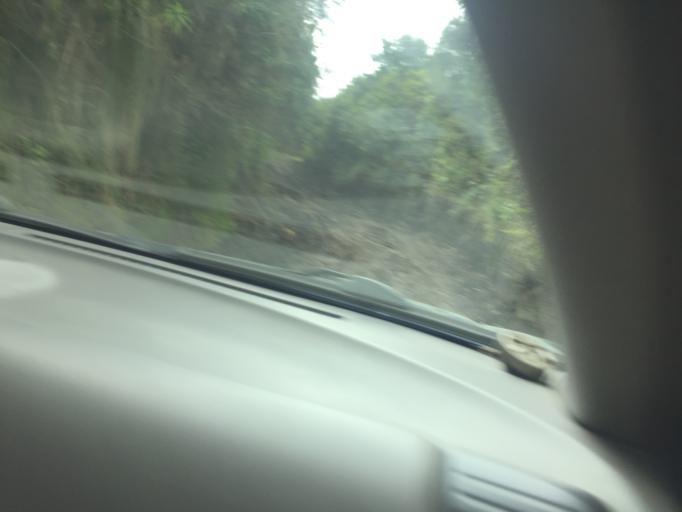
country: EC
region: Imbabura
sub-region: Canton Otavalo
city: Otavalo
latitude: 0.0861
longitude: -78.2960
